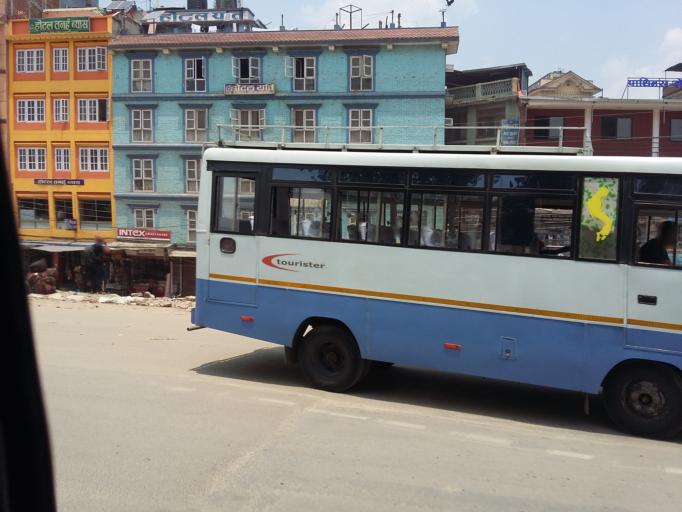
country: NP
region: Central Region
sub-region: Bagmati Zone
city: Kathmandu
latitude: 27.7351
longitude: 85.3090
